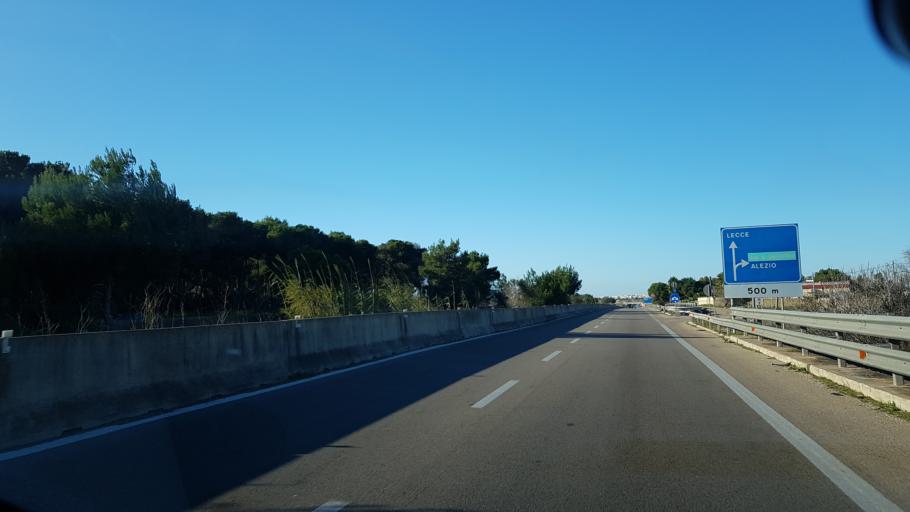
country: IT
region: Apulia
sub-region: Provincia di Lecce
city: Alezio
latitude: 40.0264
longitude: 18.0359
